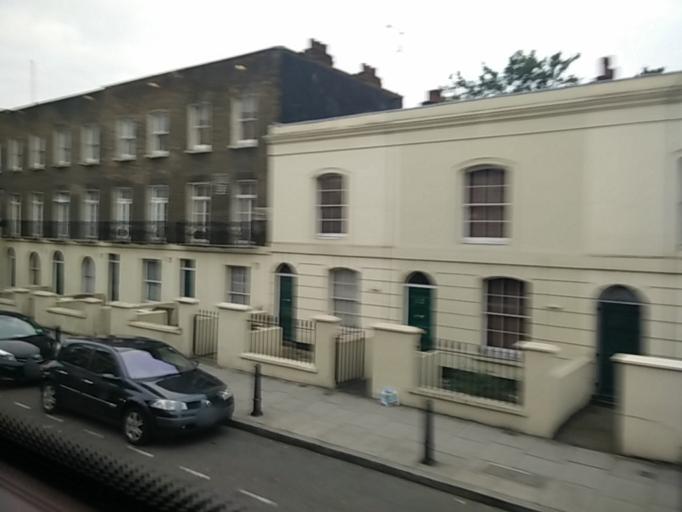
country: GB
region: England
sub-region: Greater London
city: Islington
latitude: 51.5463
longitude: -0.0790
